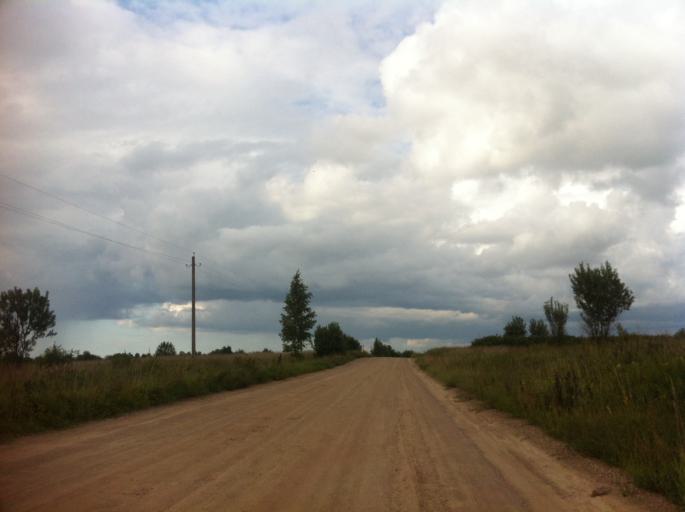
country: RU
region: Pskov
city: Izborsk
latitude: 57.8213
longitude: 27.9783
